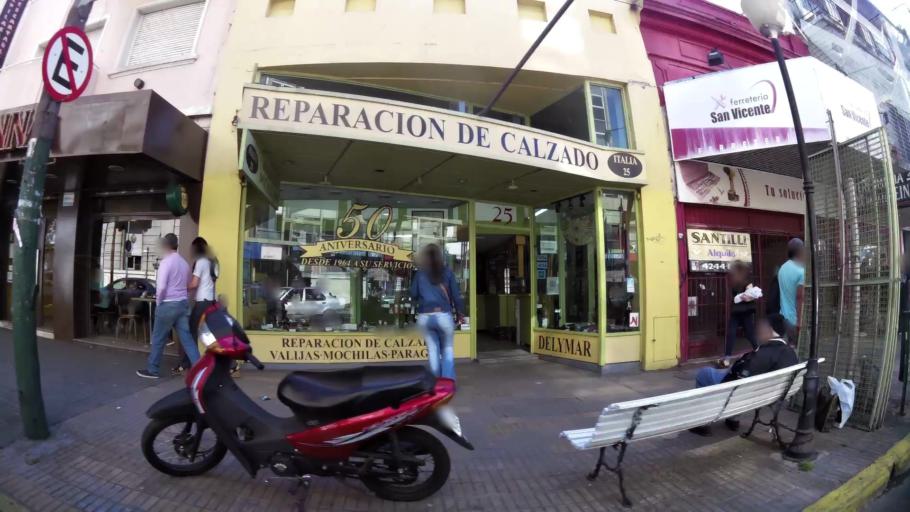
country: AR
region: Buenos Aires
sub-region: Partido de Lomas de Zamora
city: Lomas de Zamora
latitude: -34.7610
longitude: -58.4012
